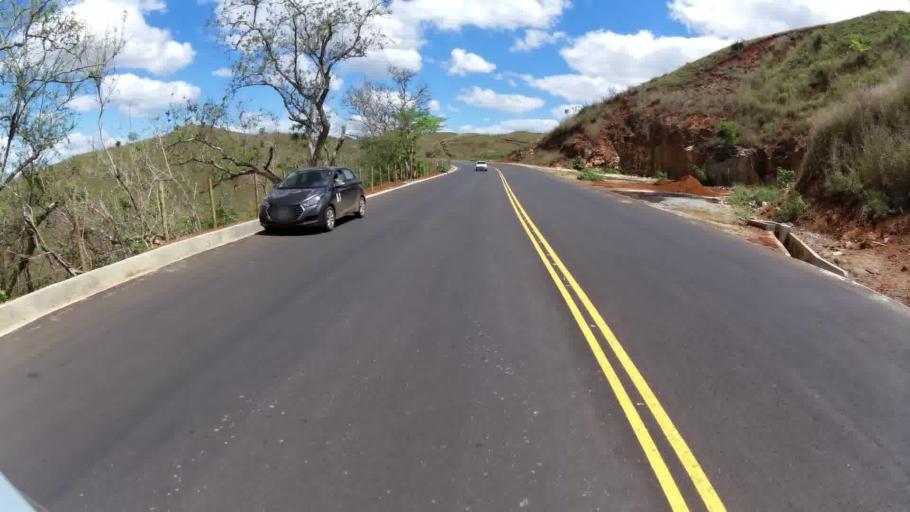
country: BR
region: Rio de Janeiro
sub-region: Itaperuna
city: Itaperuna
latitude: -21.2899
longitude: -41.8024
